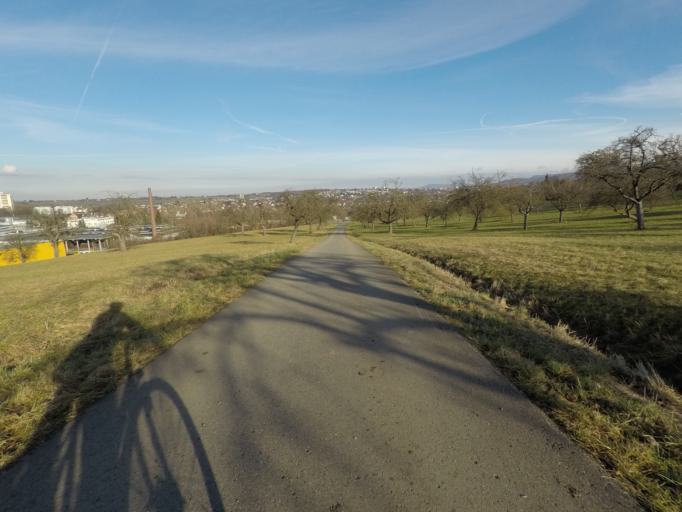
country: DE
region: Baden-Wuerttemberg
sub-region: Tuebingen Region
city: Wannweil
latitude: 48.4910
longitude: 9.1649
